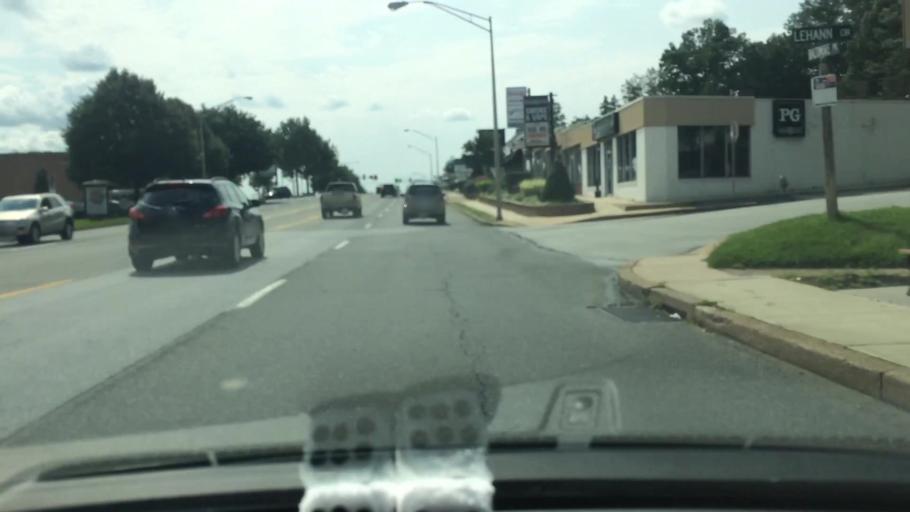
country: US
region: Pennsylvania
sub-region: Delaware County
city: Springfield
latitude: 39.9208
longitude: -75.3232
